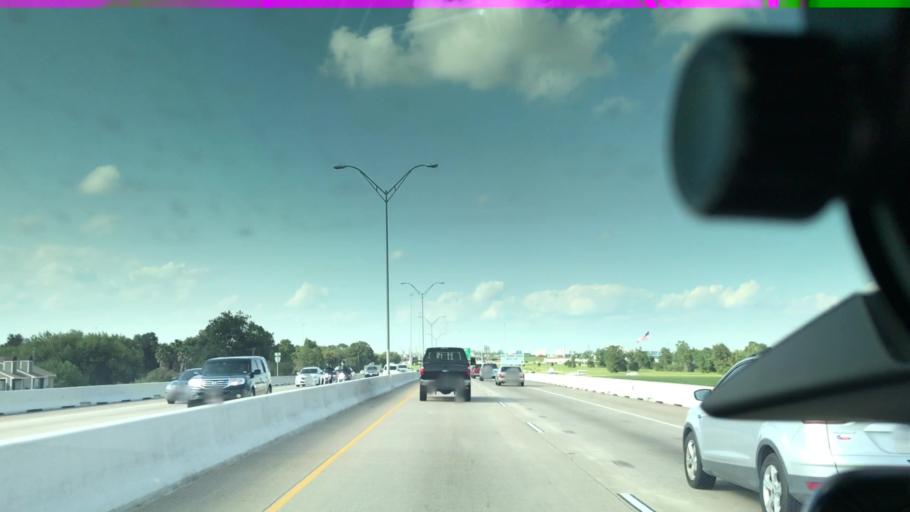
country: US
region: Texas
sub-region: Harris County
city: Deer Park
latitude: 29.7023
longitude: -95.1534
